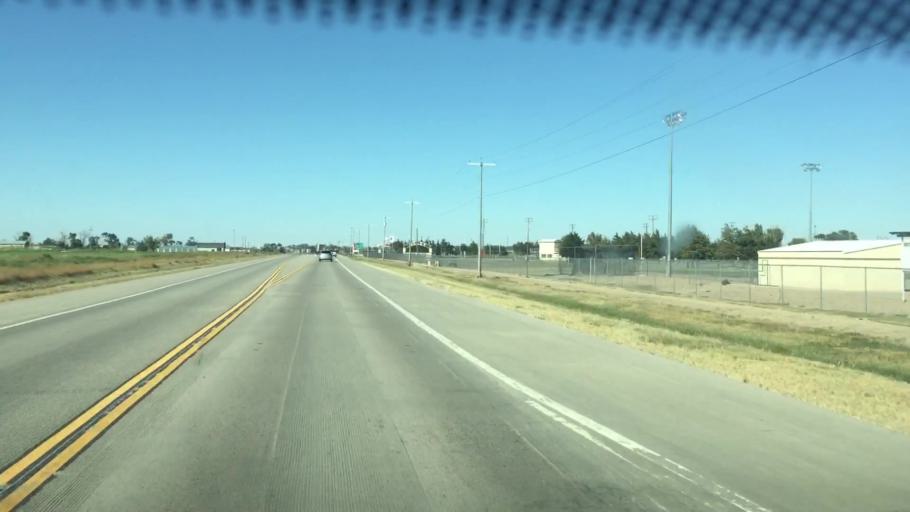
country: US
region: Colorado
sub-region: Prowers County
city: Lamar
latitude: 38.1539
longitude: -102.7237
